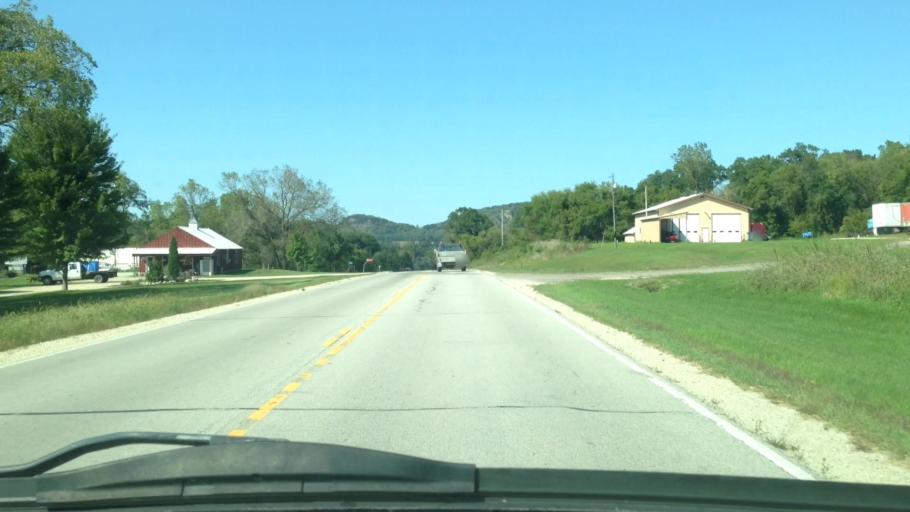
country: US
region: Minnesota
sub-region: Fillmore County
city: Rushford
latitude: 43.7836
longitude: -91.7649
